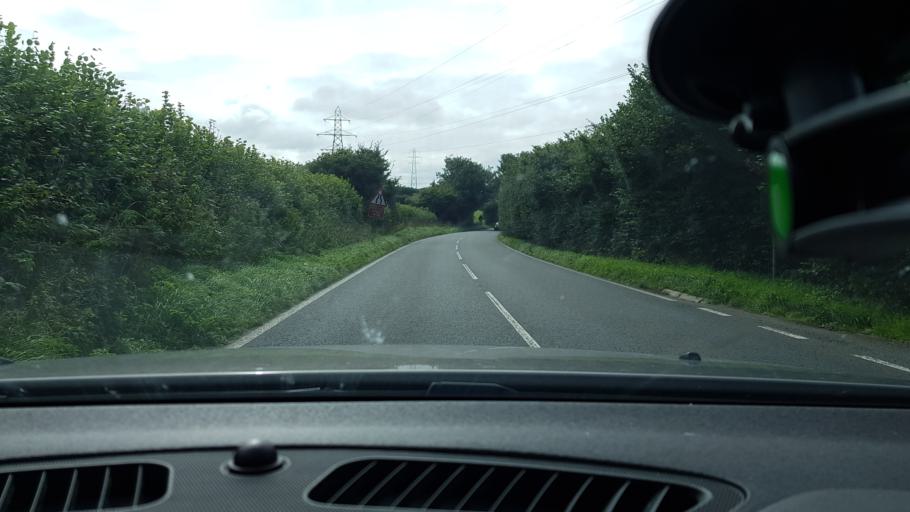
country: GB
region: England
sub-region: Cornwall
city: Camelford
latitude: 50.6036
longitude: -4.6952
